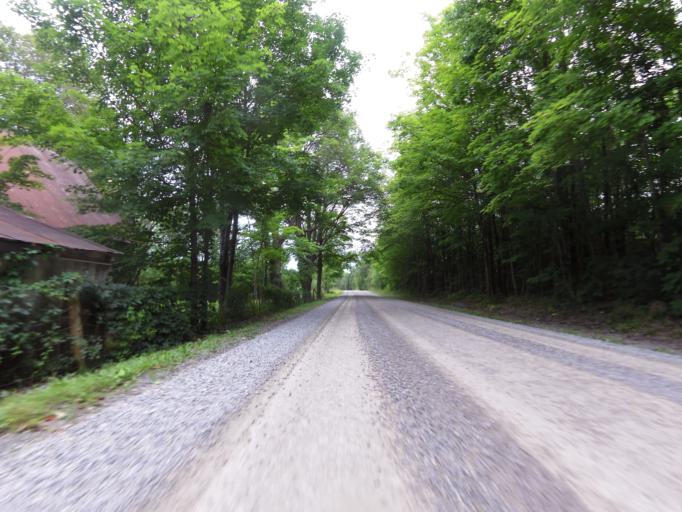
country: CA
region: Ontario
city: Carleton Place
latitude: 45.1543
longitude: -76.2090
